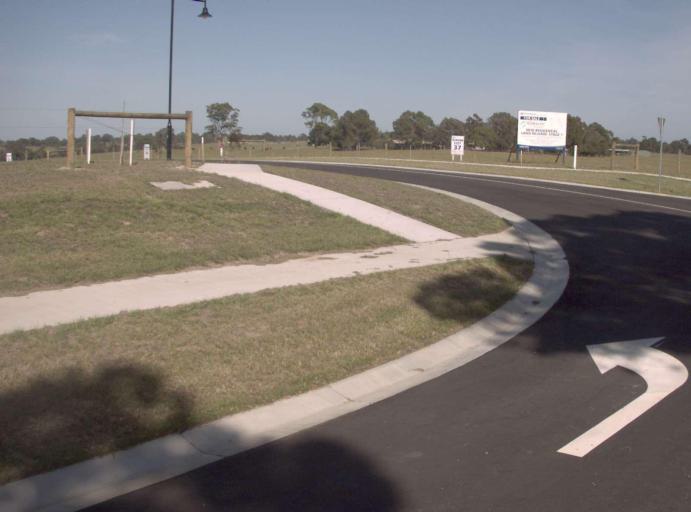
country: AU
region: Victoria
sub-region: East Gippsland
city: Lakes Entrance
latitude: -37.8207
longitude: 147.8549
